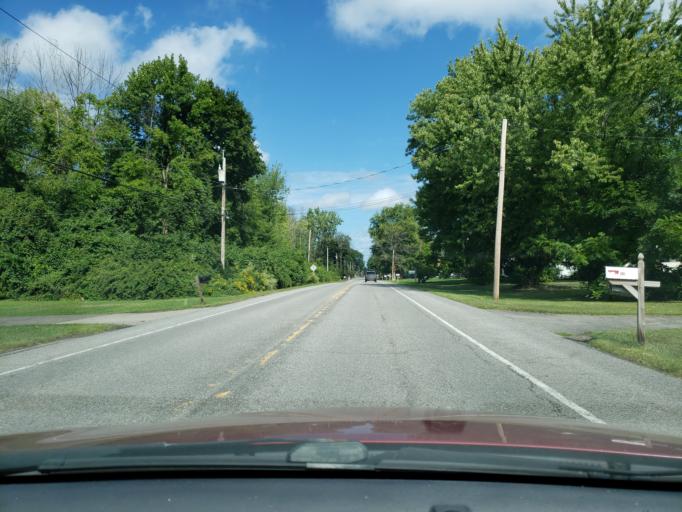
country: US
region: New York
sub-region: Monroe County
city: Greece
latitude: 43.2343
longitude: -77.7335
